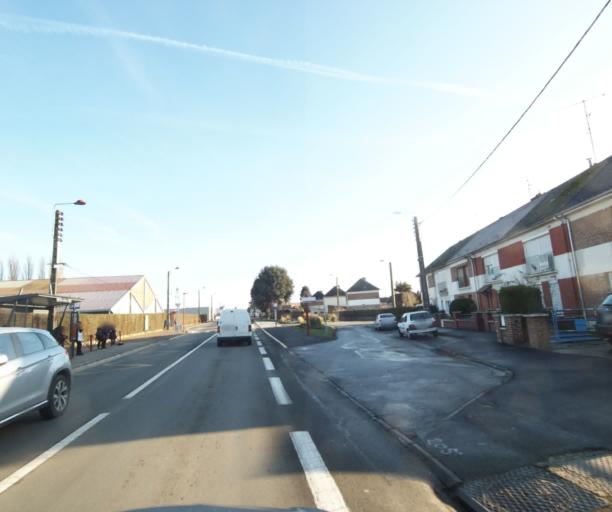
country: FR
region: Nord-Pas-de-Calais
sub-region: Departement du Nord
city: Marly
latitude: 50.3477
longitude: 3.5500
